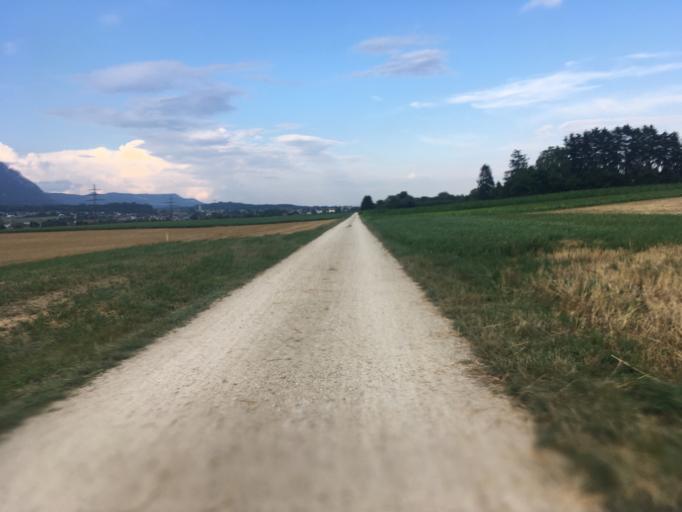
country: CH
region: Solothurn
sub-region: Bezirk Lebern
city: Selzach
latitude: 47.2023
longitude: 7.4733
